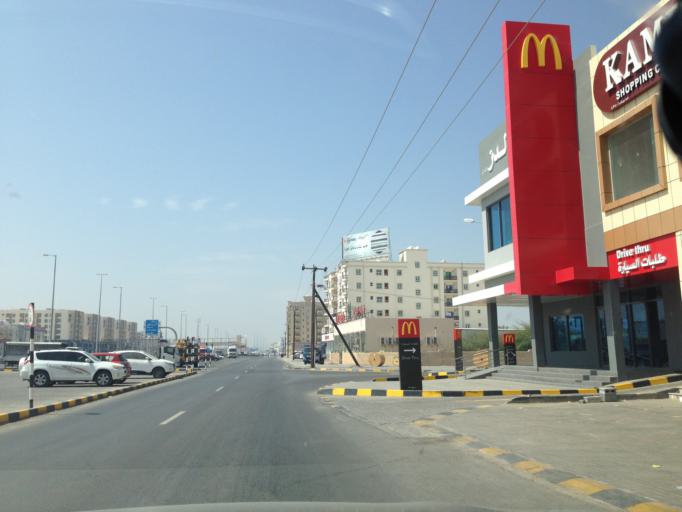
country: OM
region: Al Batinah
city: Barka'
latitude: 23.6649
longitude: 57.8976
